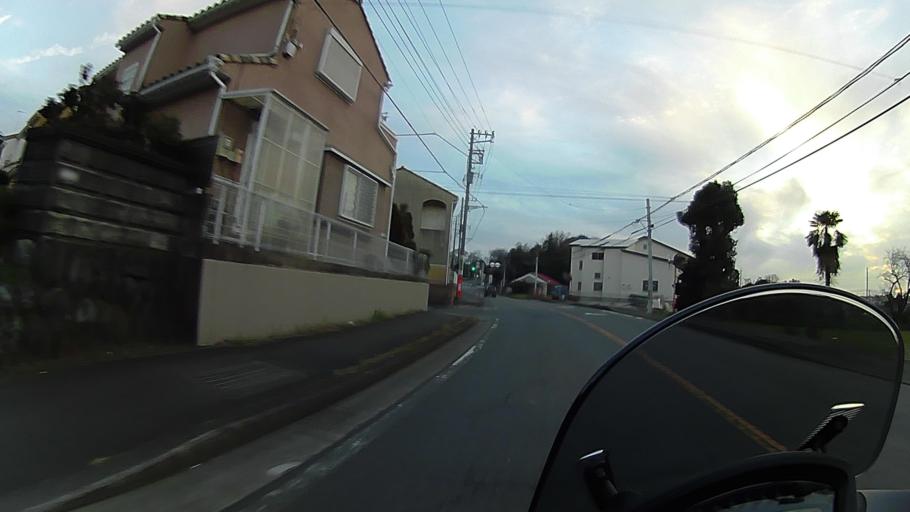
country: JP
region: Kanagawa
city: Atsugi
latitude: 35.4079
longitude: 139.4141
